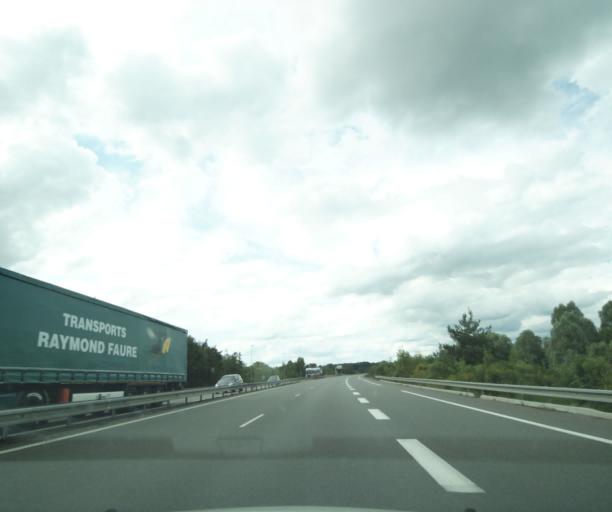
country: FR
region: Centre
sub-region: Departement du Cher
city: Vierzon
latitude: 47.2096
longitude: 2.1177
